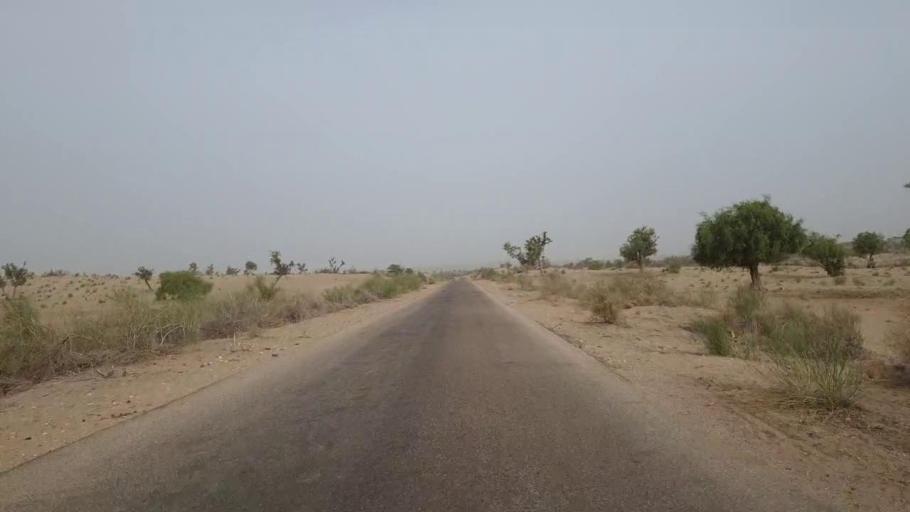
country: PK
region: Sindh
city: Islamkot
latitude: 24.5530
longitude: 70.3519
